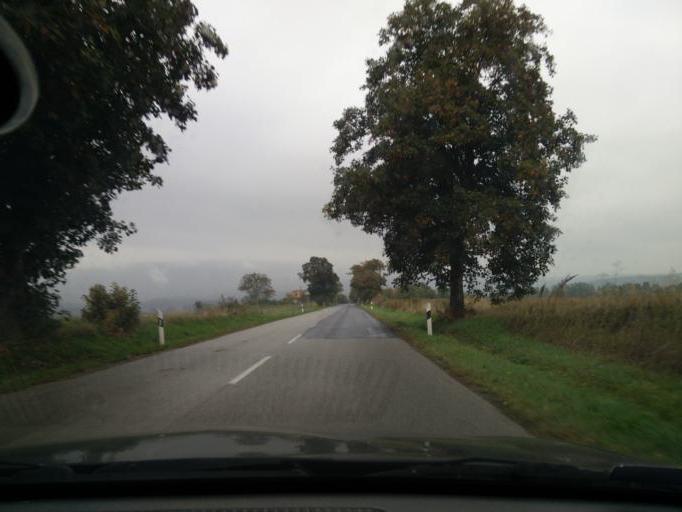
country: HU
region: Komarom-Esztergom
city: Tarjan
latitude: 47.6348
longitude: 18.5153
